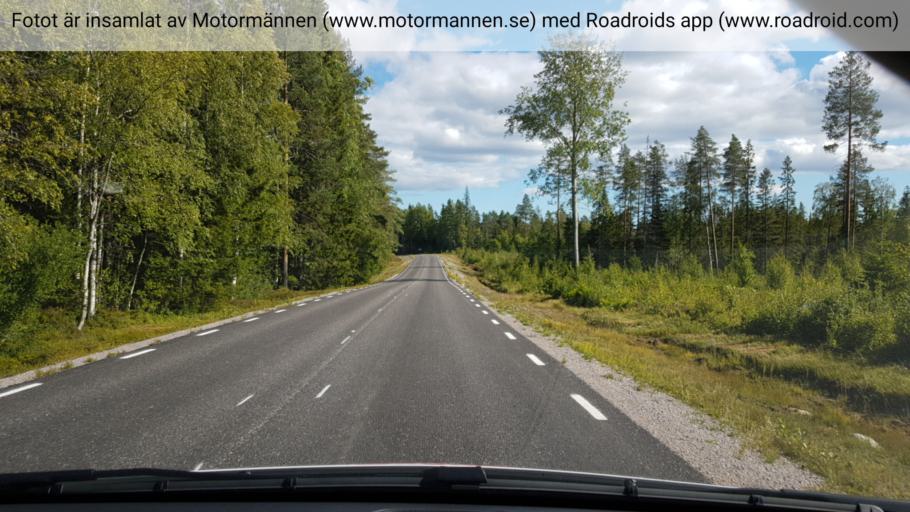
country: SE
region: Vaesterbotten
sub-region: Umea Kommun
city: Hoernefors
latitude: 63.6973
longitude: 19.7649
